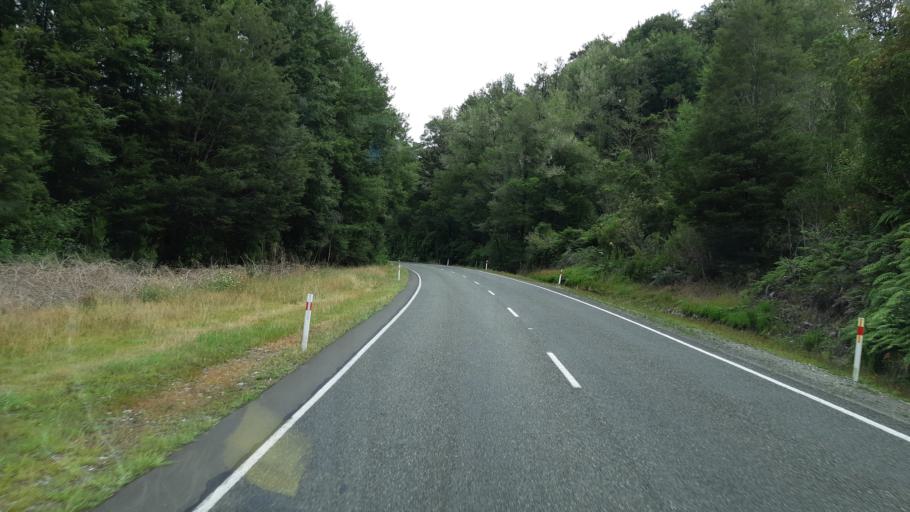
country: NZ
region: West Coast
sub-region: Buller District
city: Westport
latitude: -41.7941
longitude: 172.2172
